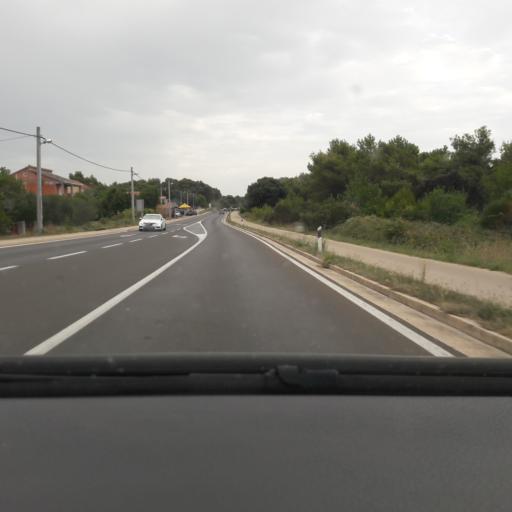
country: HR
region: Zadarska
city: Zadar
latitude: 44.1687
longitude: 15.1977
